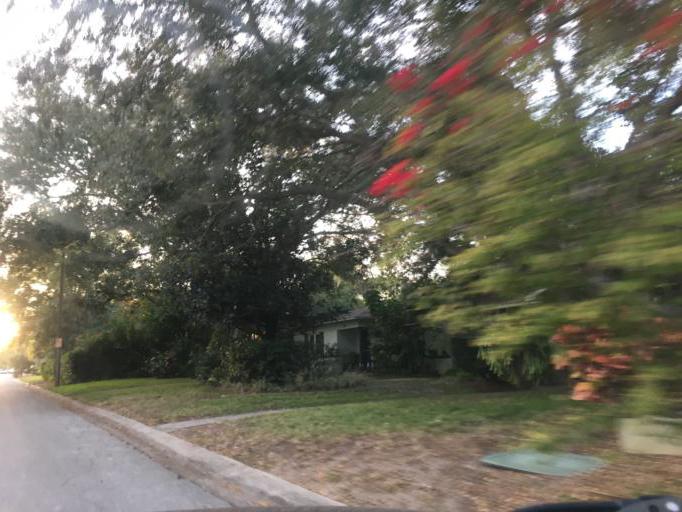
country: US
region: Florida
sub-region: Pinellas County
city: Saint Petersburg
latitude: 27.7939
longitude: -82.6367
